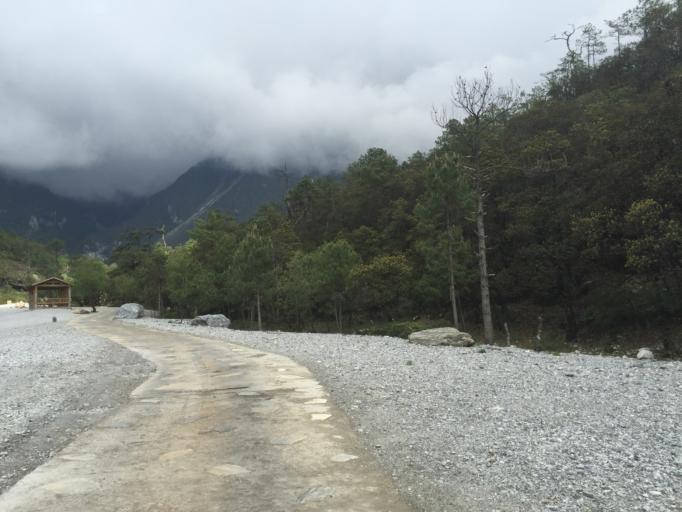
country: CN
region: Yunnan
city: Xiaqiaotou
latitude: 27.1296
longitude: 100.2375
